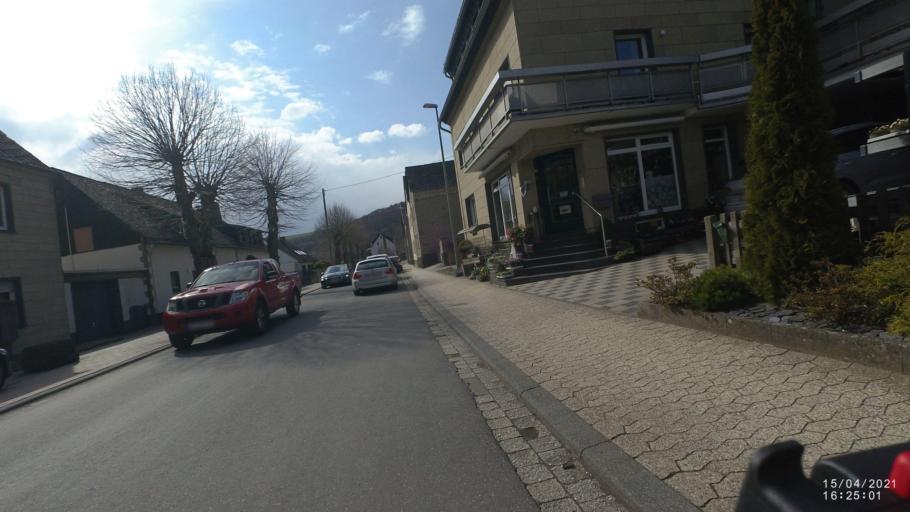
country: DE
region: Rheinland-Pfalz
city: Rieden
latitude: 50.3943
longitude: 7.1727
